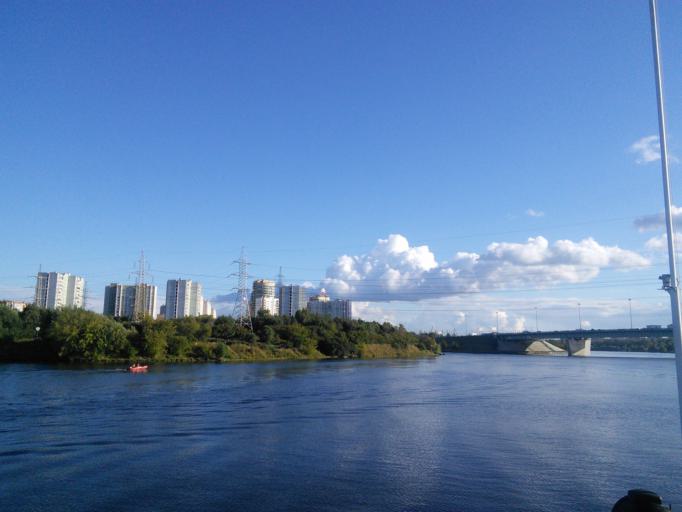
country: RU
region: Moskovskaya
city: Levoberezhnaya
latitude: 55.8775
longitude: 37.4583
